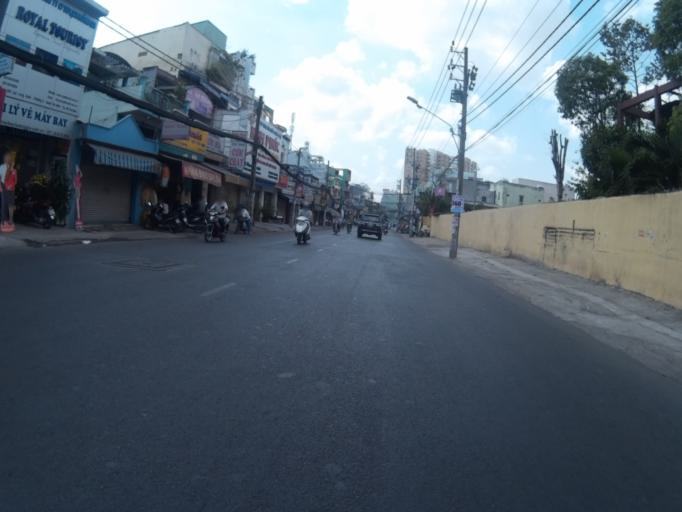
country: VN
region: Ho Chi Minh City
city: Quan Tan Phu
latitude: 10.7796
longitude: 106.6506
